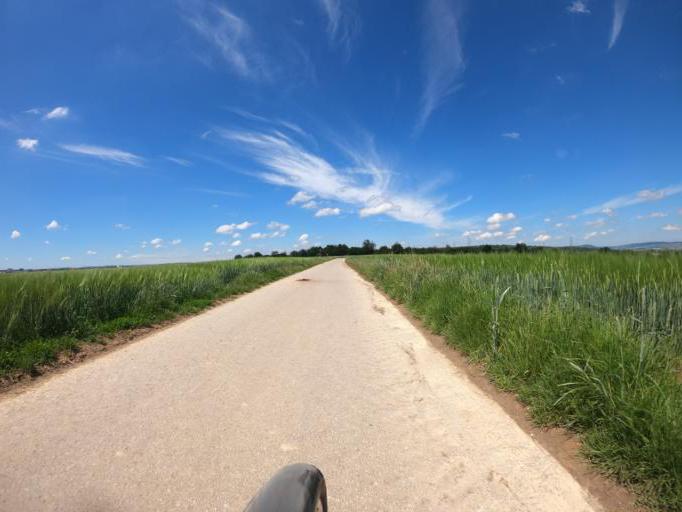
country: DE
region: Baden-Wuerttemberg
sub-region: Regierungsbezirk Stuttgart
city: Tamm
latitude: 48.9158
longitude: 9.1131
